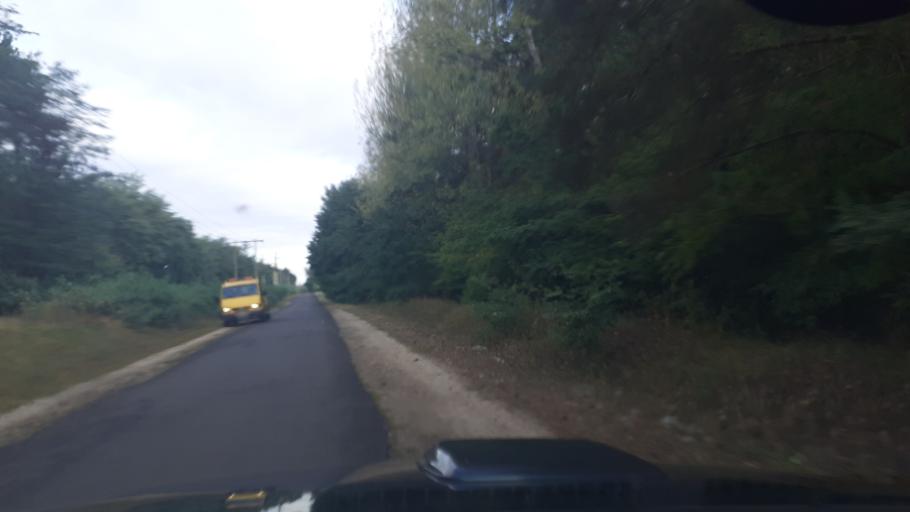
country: HU
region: Fejer
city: dunaujvaros
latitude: 46.9440
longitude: 18.8630
